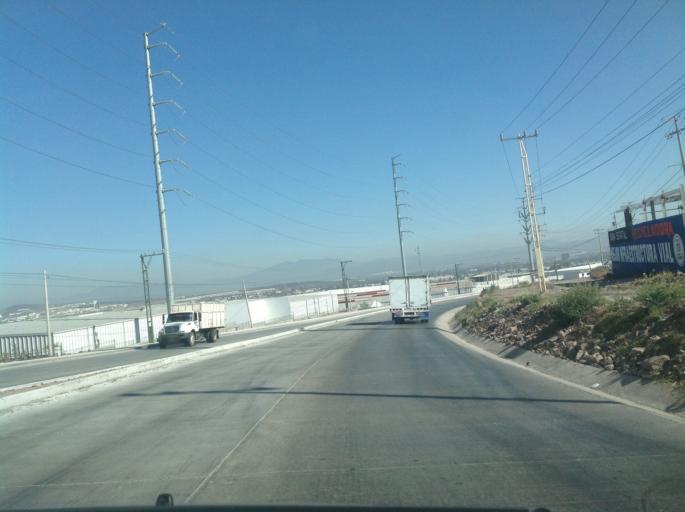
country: MX
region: Queretaro
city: El Colorado
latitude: 20.5652
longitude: -100.2678
